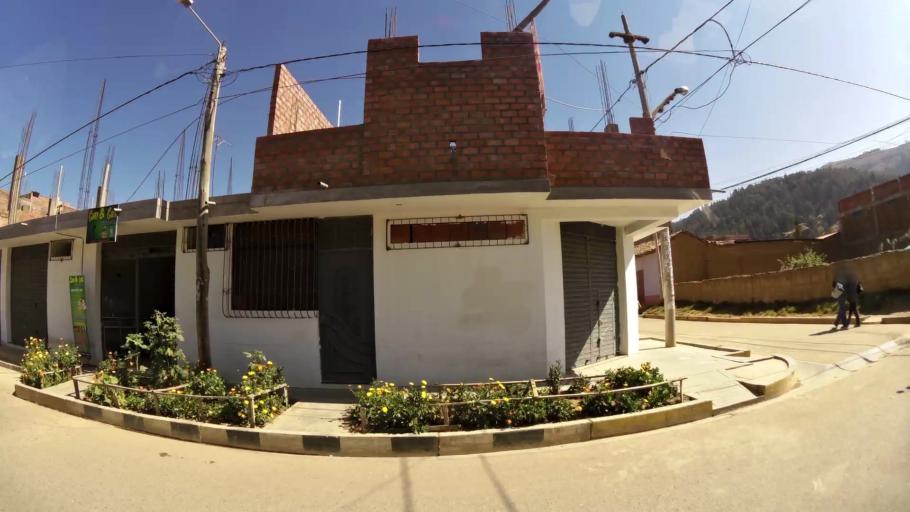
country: PE
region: Junin
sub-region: Provincia de Huancayo
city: San Jeronimo
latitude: -11.9496
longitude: -75.2838
